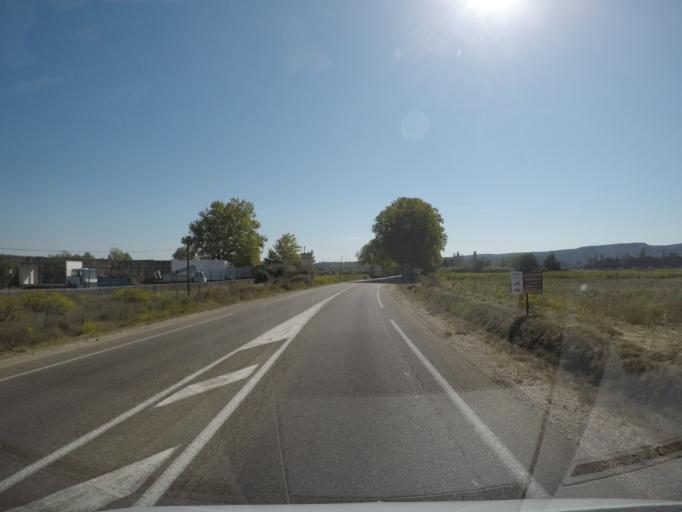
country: FR
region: Languedoc-Roussillon
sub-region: Departement du Gard
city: Castillon-du-Gard
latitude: 43.9652
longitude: 4.5113
